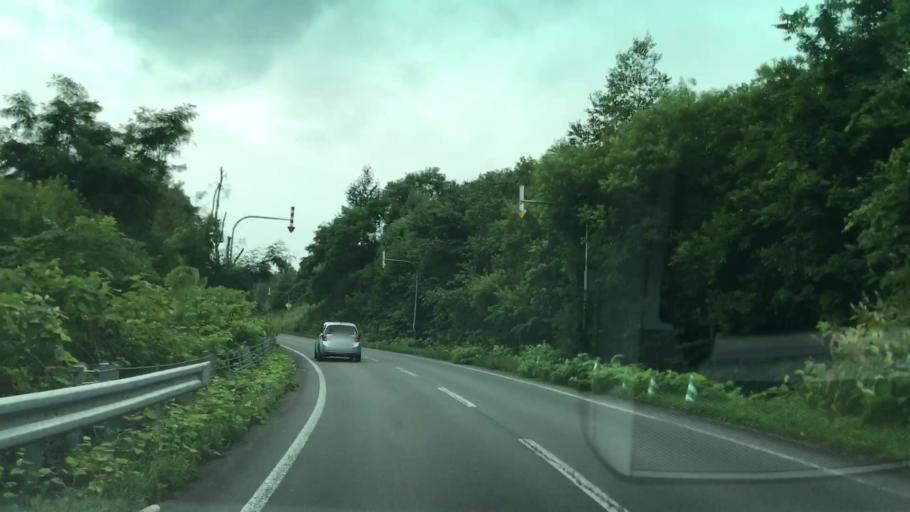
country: JP
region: Hokkaido
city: Yoichi
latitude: 43.1425
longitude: 140.8205
